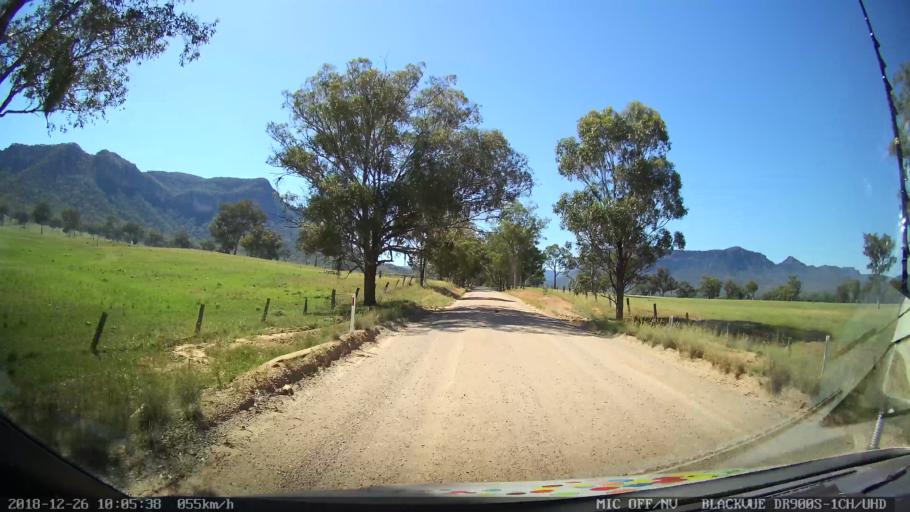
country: AU
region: New South Wales
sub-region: Mid-Western Regional
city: Kandos
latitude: -33.0788
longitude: 150.2121
